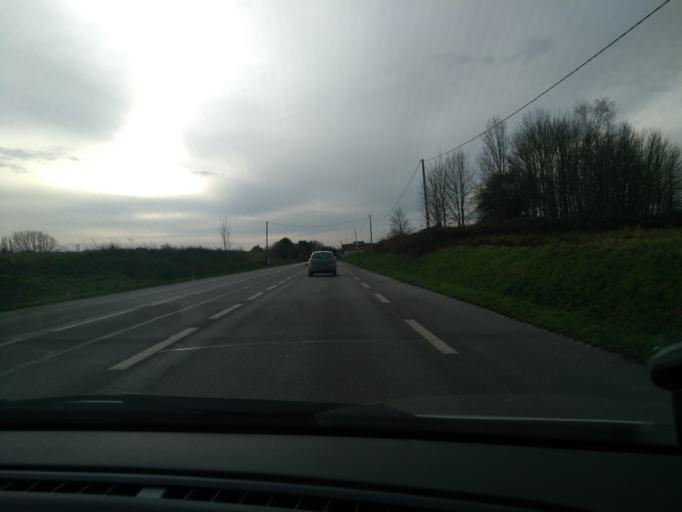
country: FR
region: Nord-Pas-de-Calais
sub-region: Departement du Nord
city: Maubeuge
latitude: 50.3177
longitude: 3.9768
